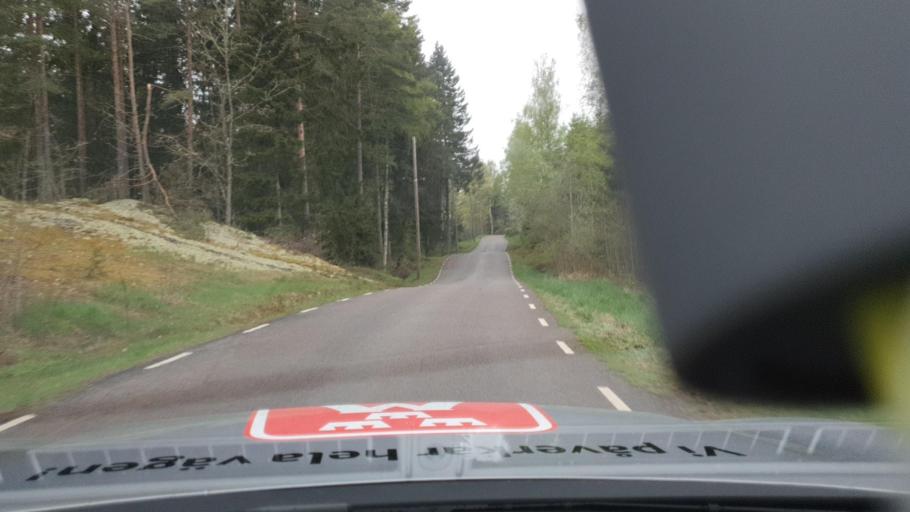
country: SE
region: Kalmar
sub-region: Vasterviks Kommun
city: Ankarsrum
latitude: 57.7818
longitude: 16.1485
